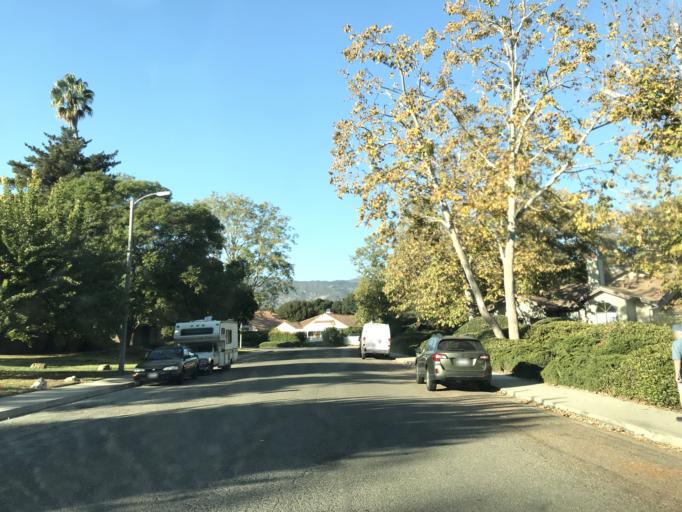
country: US
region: California
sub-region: Santa Barbara County
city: Goleta
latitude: 34.4502
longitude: -119.8109
